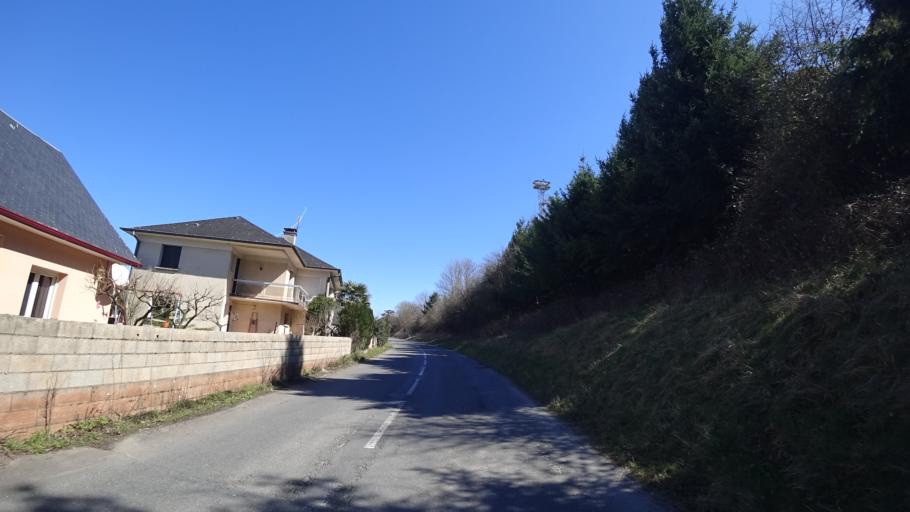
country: FR
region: Midi-Pyrenees
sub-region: Departement de l'Aveyron
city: Rodez
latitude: 44.3634
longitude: 2.5786
